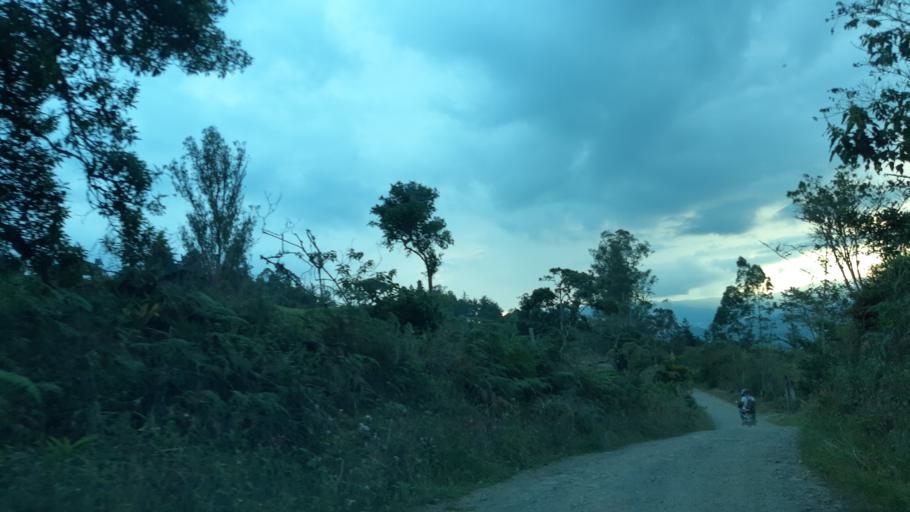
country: CO
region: Boyaca
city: Garagoa
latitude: 5.1104
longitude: -73.3532
